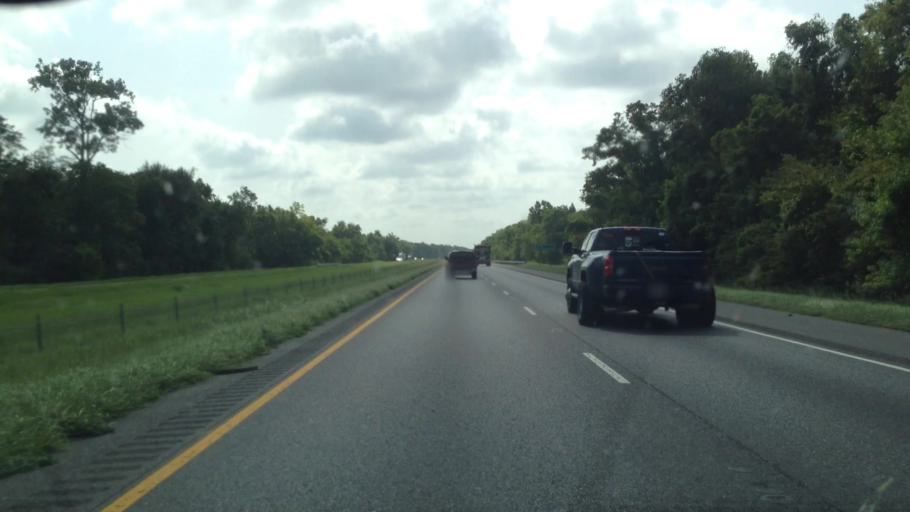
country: US
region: Louisiana
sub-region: Ascension Parish
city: Sorrento
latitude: 30.1512
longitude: -90.7916
